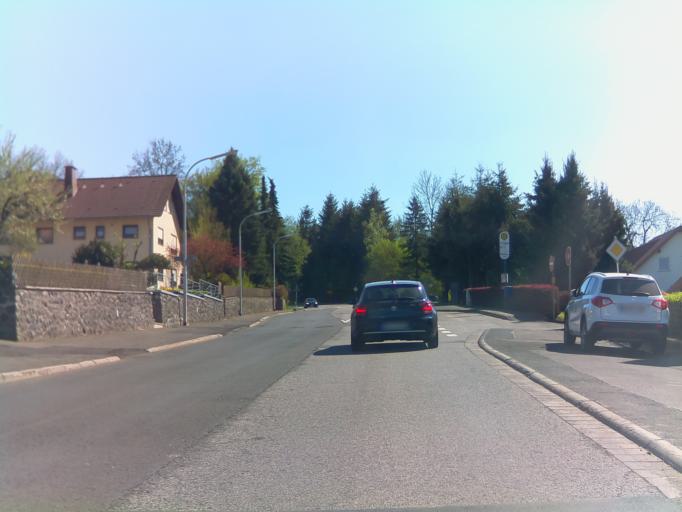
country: DE
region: Hesse
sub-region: Regierungsbezirk Giessen
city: Lauterbach
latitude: 50.6169
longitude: 9.3890
